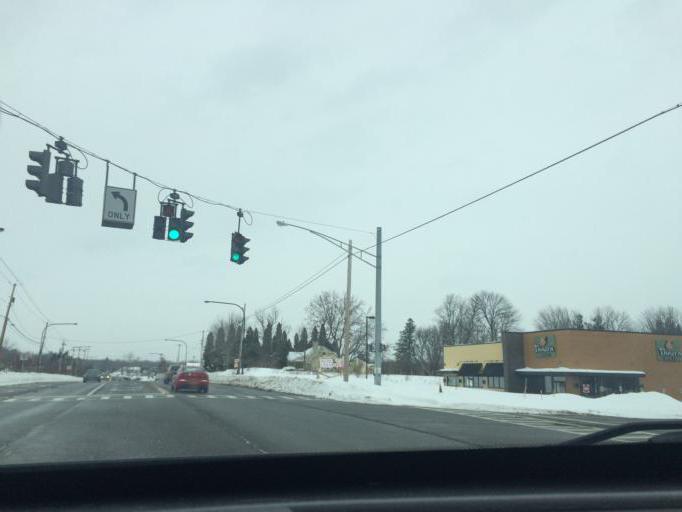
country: US
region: New York
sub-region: Monroe County
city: Fairport
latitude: 43.1273
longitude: -77.4412
